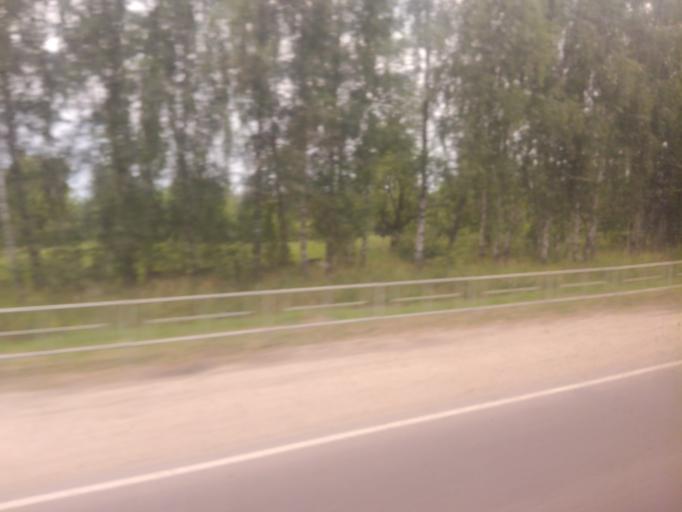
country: RU
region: Kursk
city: Kursk
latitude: 51.7534
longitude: 36.1057
